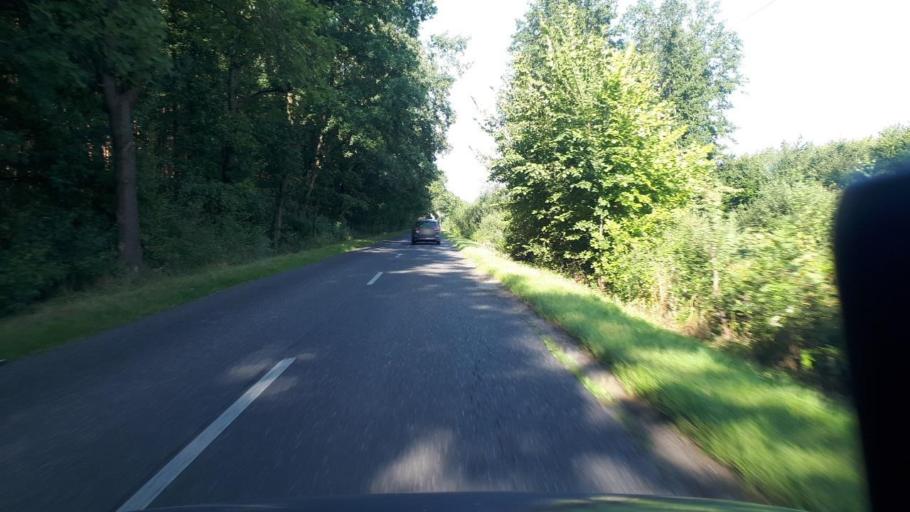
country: PL
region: Silesian Voivodeship
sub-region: Powiat tarnogorski
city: Tworog
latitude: 50.4835
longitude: 18.6913
